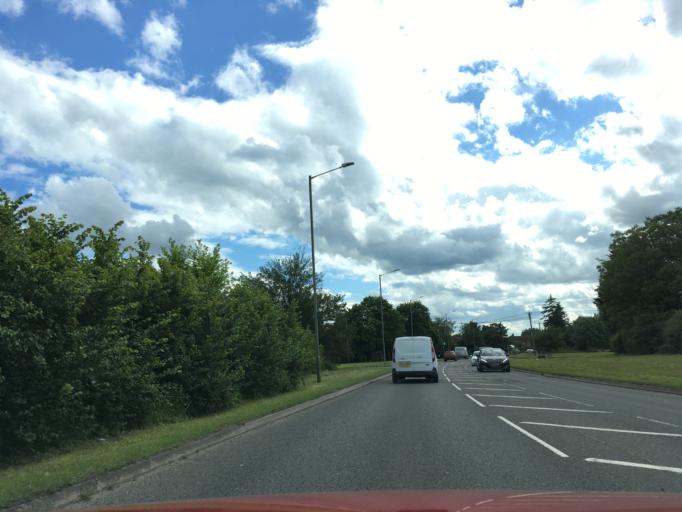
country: GB
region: England
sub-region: Buckinghamshire
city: Aylesbury
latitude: 51.8364
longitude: -0.7733
